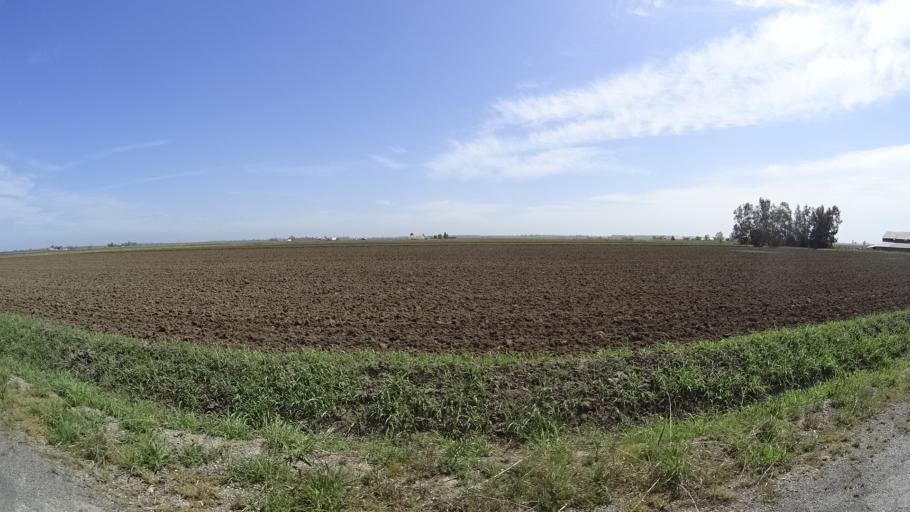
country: US
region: California
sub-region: Glenn County
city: Hamilton City
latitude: 39.5991
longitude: -122.0466
